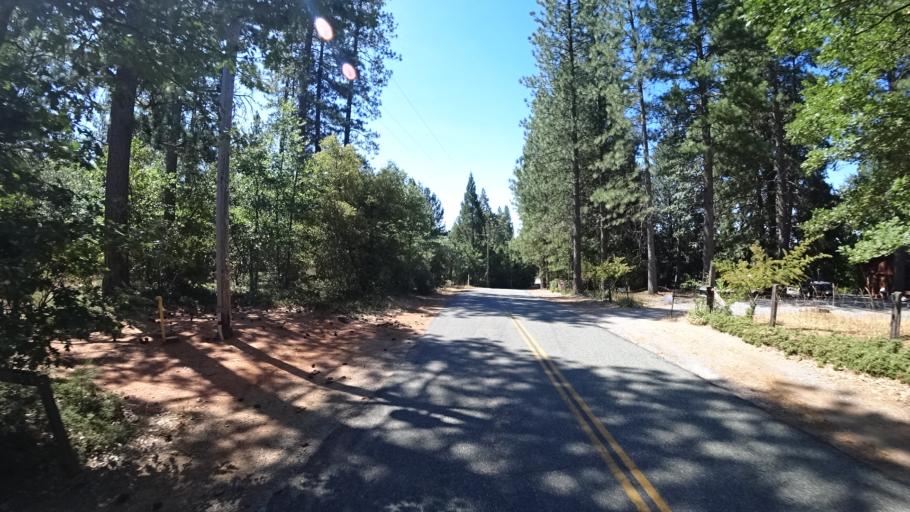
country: US
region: California
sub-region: Amador County
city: Pioneer
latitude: 38.4022
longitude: -120.5058
